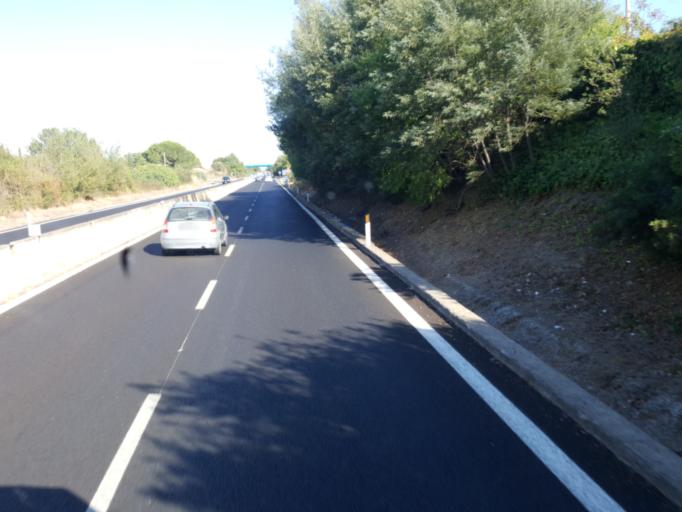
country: IT
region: Latium
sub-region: Provincia di Viterbo
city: Pescia Romana
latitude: 42.3965
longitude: 11.5199
